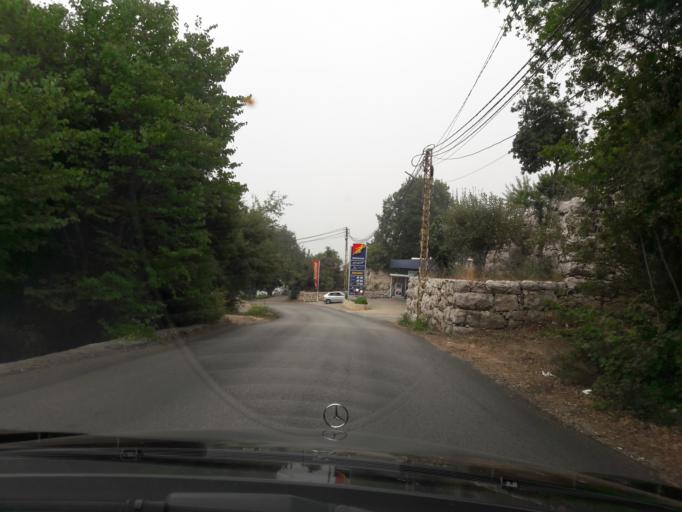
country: LB
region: Mont-Liban
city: Djounie
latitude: 33.9887
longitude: 35.6793
